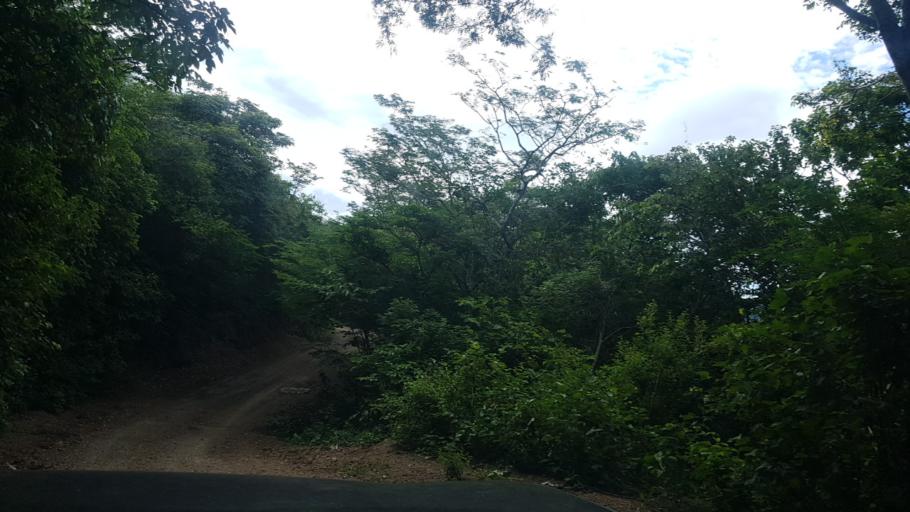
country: NI
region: Nueva Segovia
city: Ocotal
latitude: 13.6002
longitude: -86.4265
